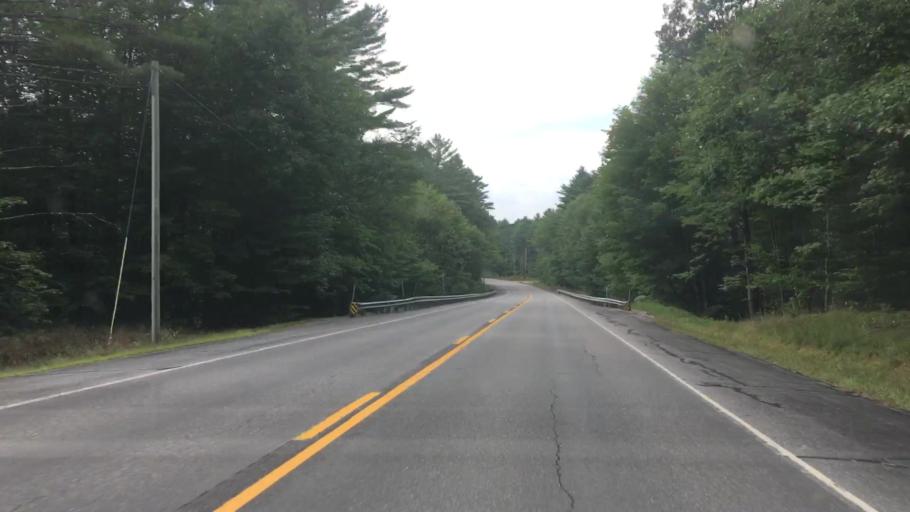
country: US
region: Maine
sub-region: Oxford County
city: Bethel
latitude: 44.4865
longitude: -70.7467
